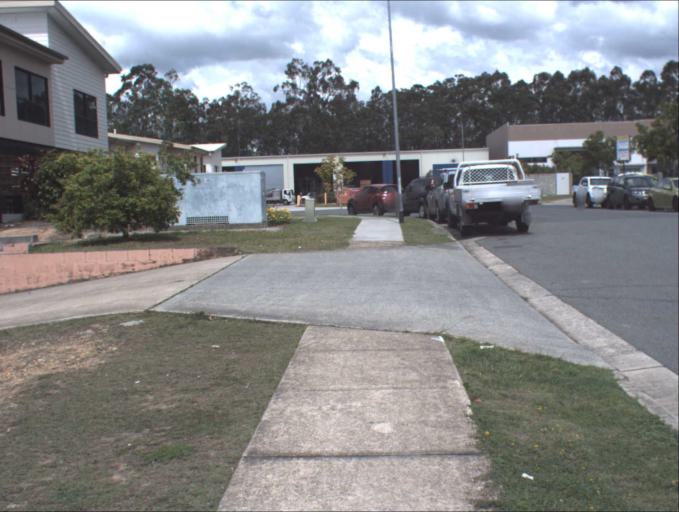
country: AU
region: Queensland
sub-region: Brisbane
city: Sunnybank Hills
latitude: -27.6647
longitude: 153.0474
